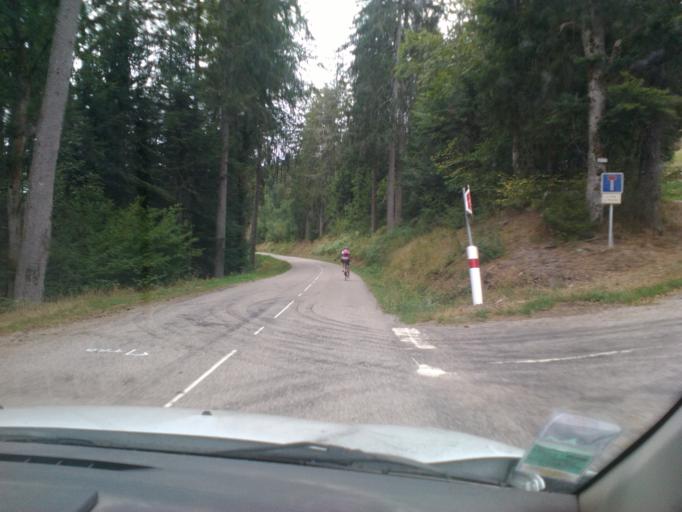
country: FR
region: Lorraine
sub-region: Departement des Vosges
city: Le Tholy
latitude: 48.1079
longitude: 6.7561
